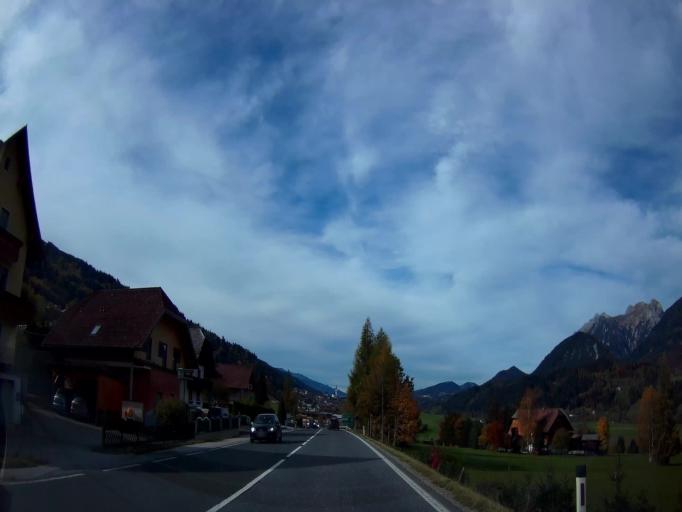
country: AT
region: Styria
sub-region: Politischer Bezirk Liezen
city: Haus im Ennstal
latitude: 47.4127
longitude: 13.7870
